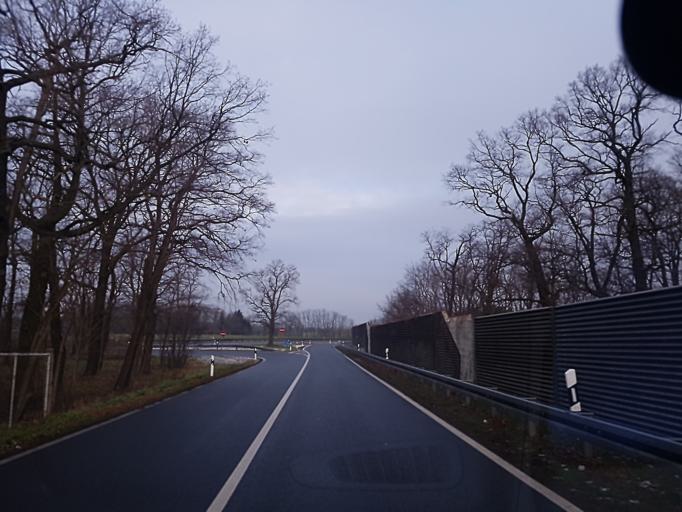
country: DE
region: Brandenburg
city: Calau
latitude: 51.7853
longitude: 13.8784
